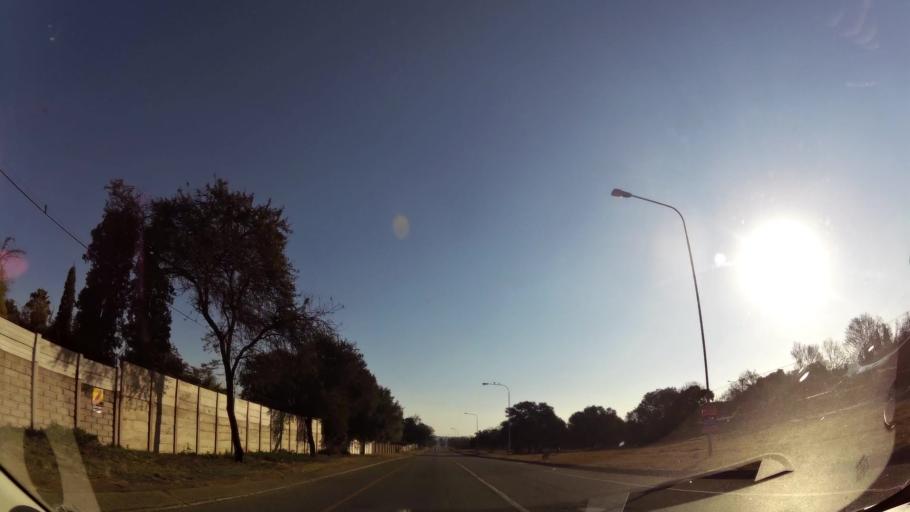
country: ZA
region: Gauteng
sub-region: City of Tshwane Metropolitan Municipality
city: Centurion
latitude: -25.8684
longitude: 28.1493
